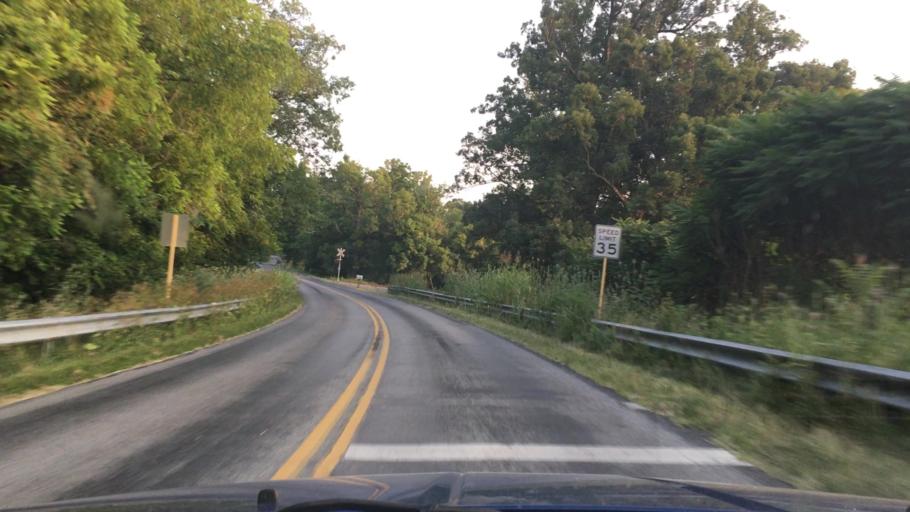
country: US
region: Virginia
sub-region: Augusta County
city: Verona
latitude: 38.2376
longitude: -78.9676
